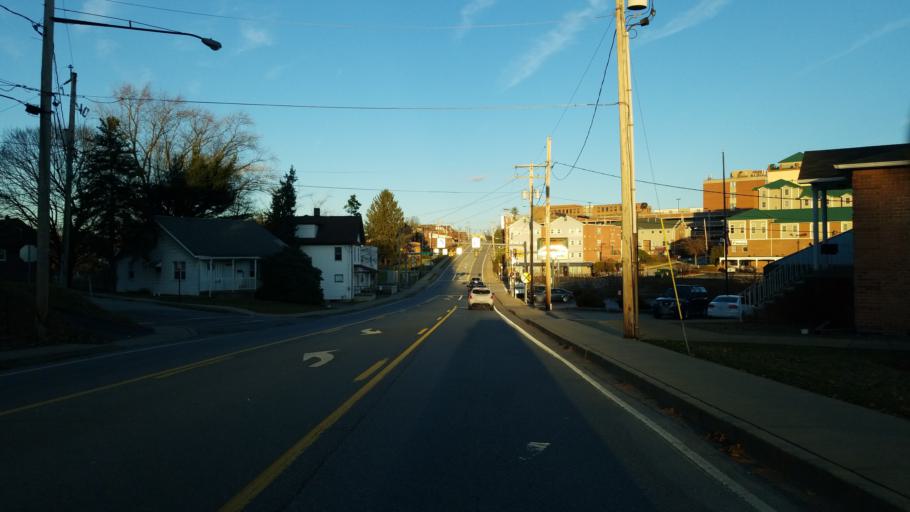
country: US
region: Pennsylvania
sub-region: Indiana County
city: Indiana
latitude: 40.6161
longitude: -79.1651
